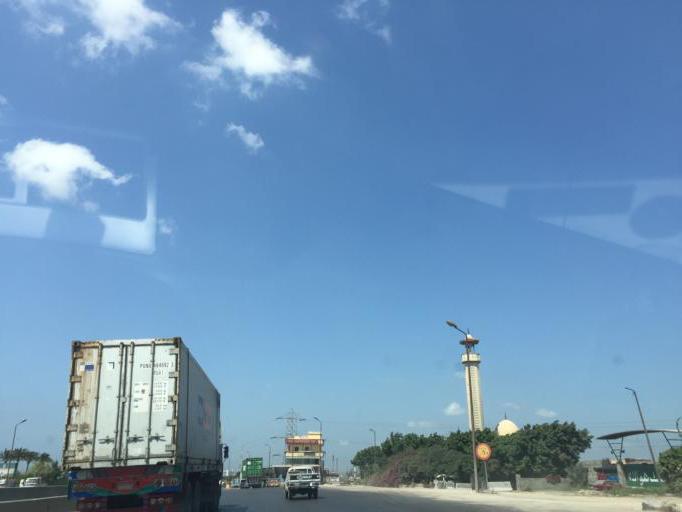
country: EG
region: Alexandria
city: Alexandria
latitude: 31.0860
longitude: 29.8503
